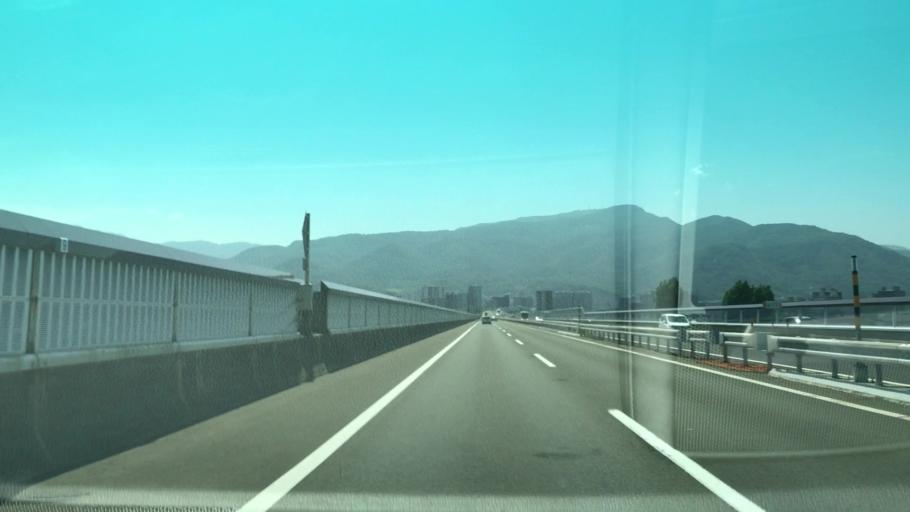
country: JP
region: Hokkaido
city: Sapporo
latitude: 43.0965
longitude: 141.2952
